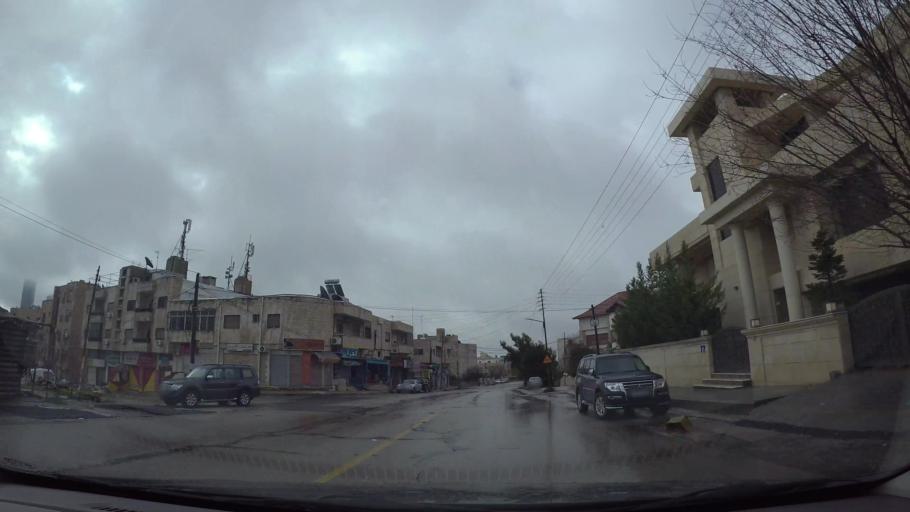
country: JO
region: Amman
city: Wadi as Sir
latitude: 31.9708
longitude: 35.8567
